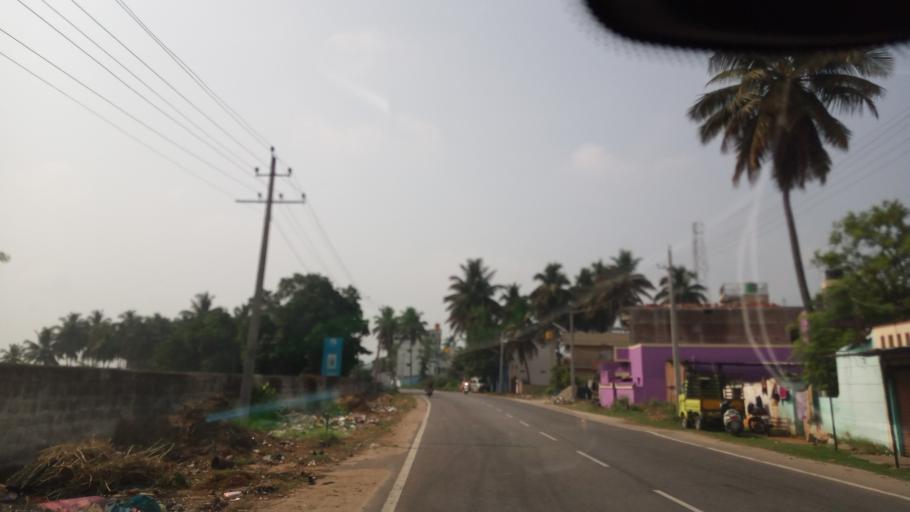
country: IN
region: Karnataka
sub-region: Mandya
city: Pandavapura
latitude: 12.5059
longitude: 76.6752
